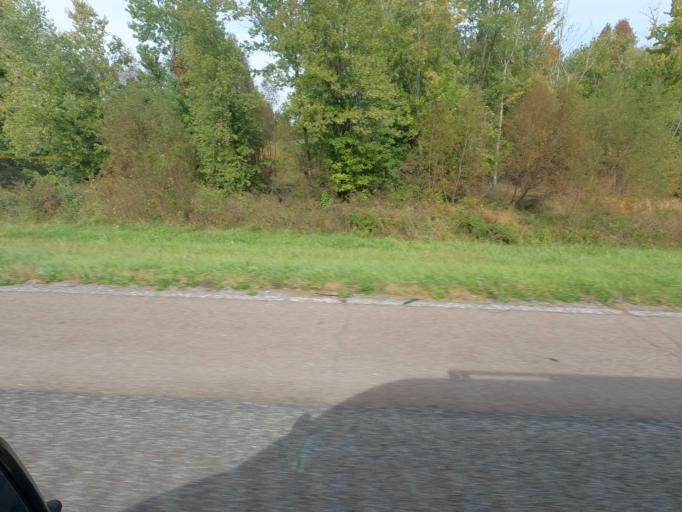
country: US
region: Tennessee
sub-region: Henderson County
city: Lexington
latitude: 35.7480
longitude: -88.5527
